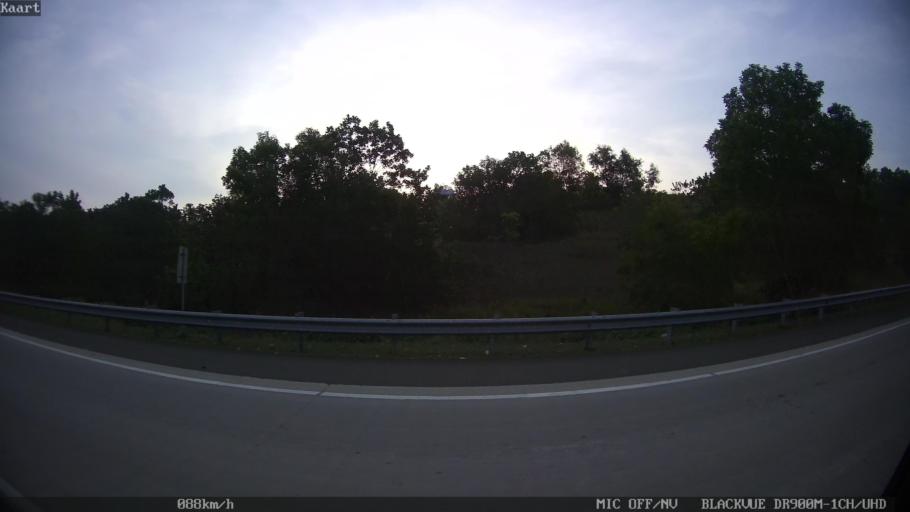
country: ID
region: Lampung
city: Penengahan
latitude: -5.8449
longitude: 105.7270
